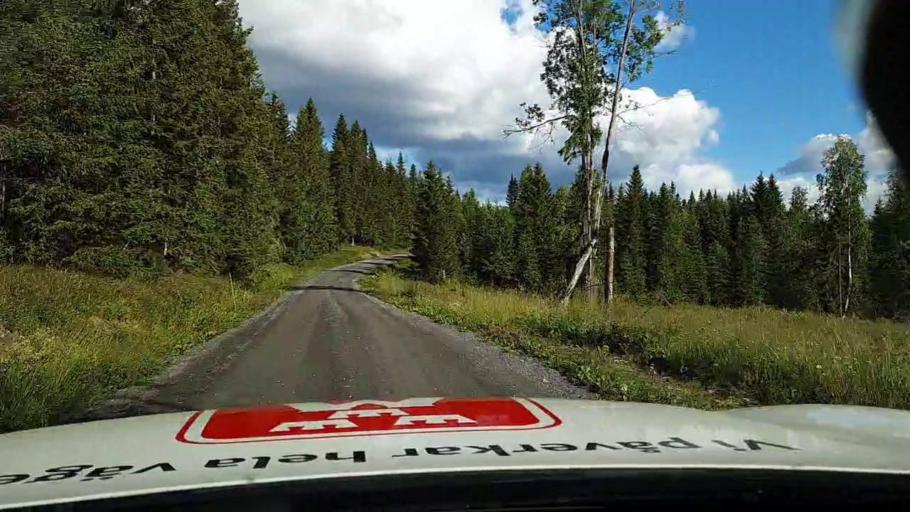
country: SE
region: Jaemtland
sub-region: Krokoms Kommun
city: Valla
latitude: 63.3178
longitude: 13.7689
